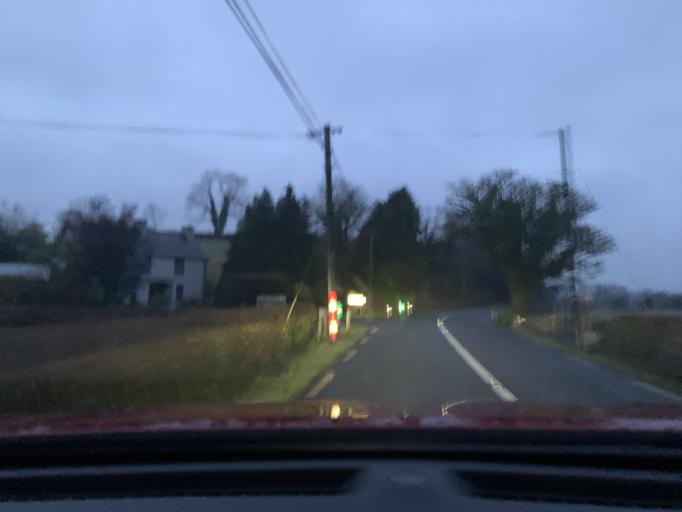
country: IE
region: Connaught
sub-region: Sligo
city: Ballymote
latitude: 54.0478
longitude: -8.5239
